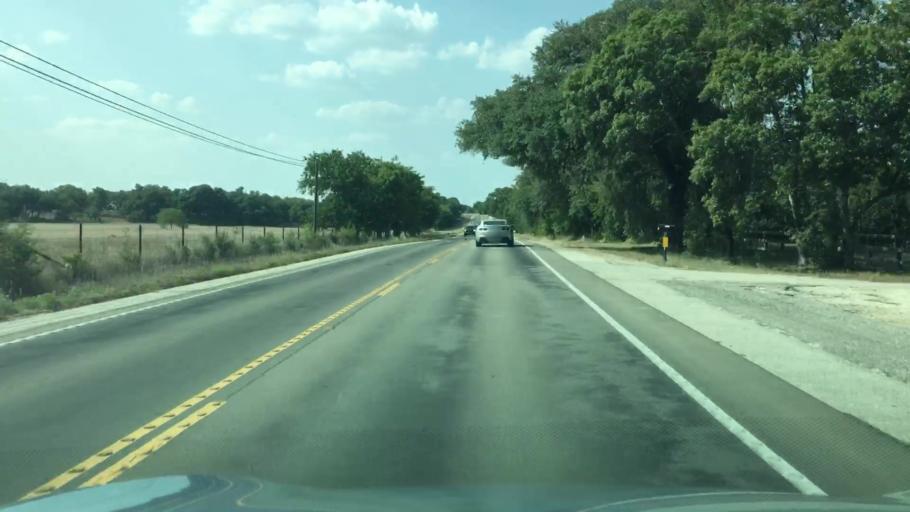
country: US
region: Texas
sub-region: Hays County
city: Dripping Springs
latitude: 30.1410
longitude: -98.0886
